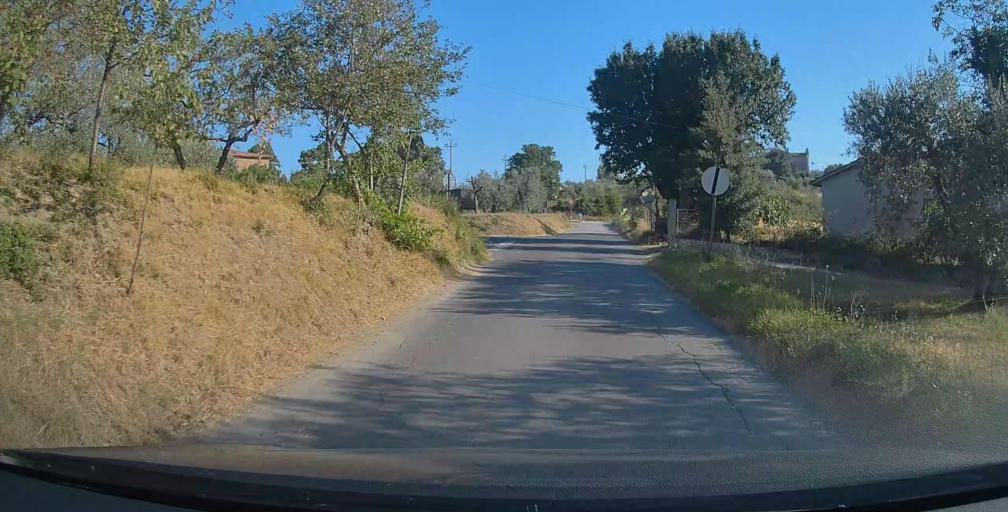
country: IT
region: Umbria
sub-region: Provincia di Terni
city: Calvi dell'Umbria
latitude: 42.3906
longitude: 12.5672
